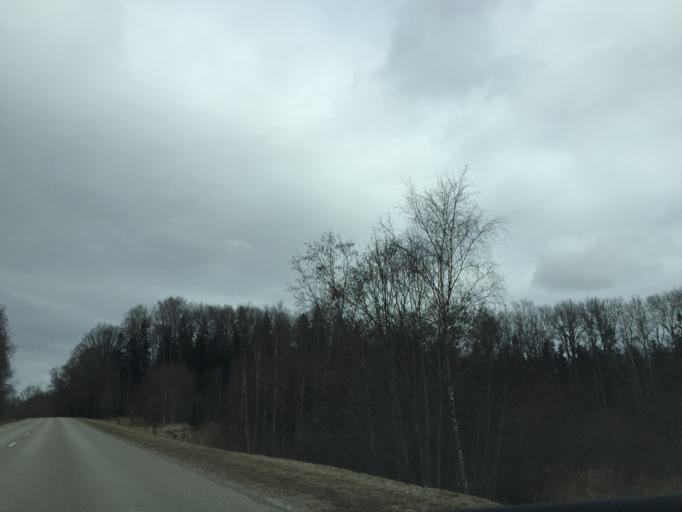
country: LV
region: Kraslavas Rajons
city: Kraslava
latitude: 55.9483
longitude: 27.1630
